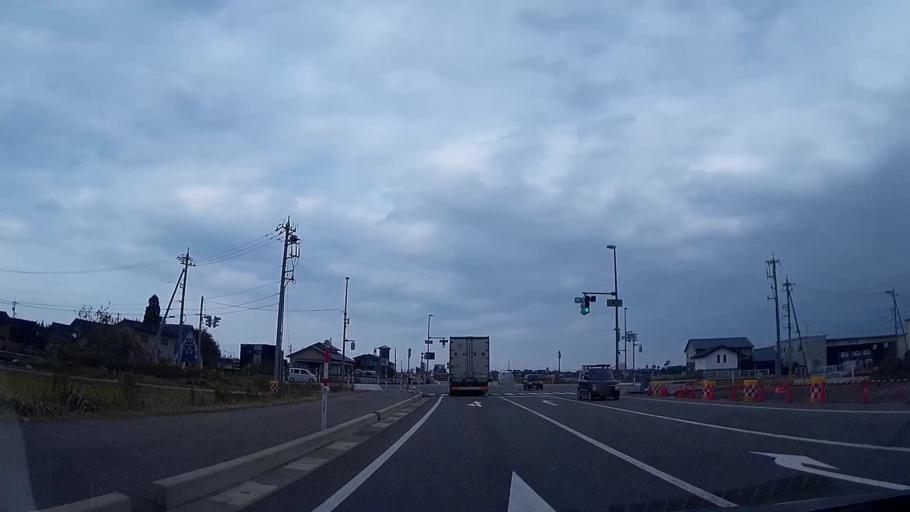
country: JP
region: Toyama
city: Nyuzen
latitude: 36.8916
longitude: 137.4442
